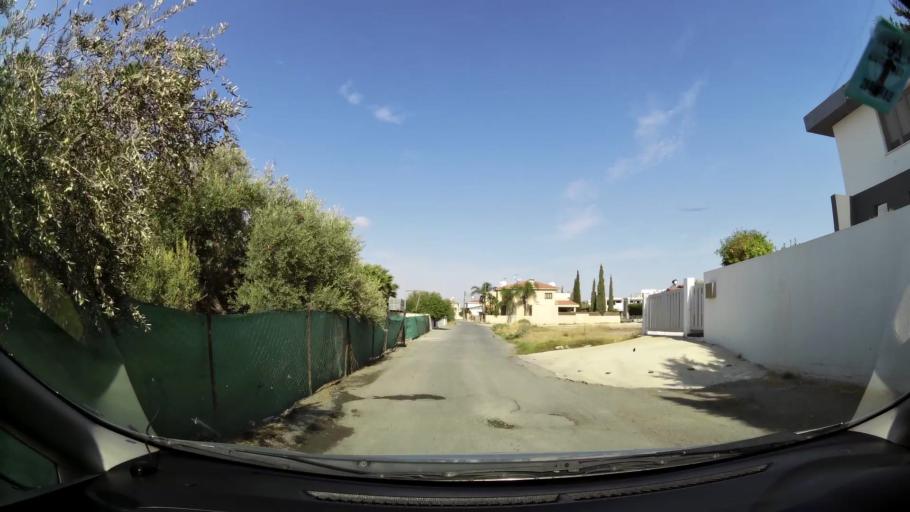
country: CY
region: Larnaka
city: Aradippou
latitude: 34.9426
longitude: 33.5863
